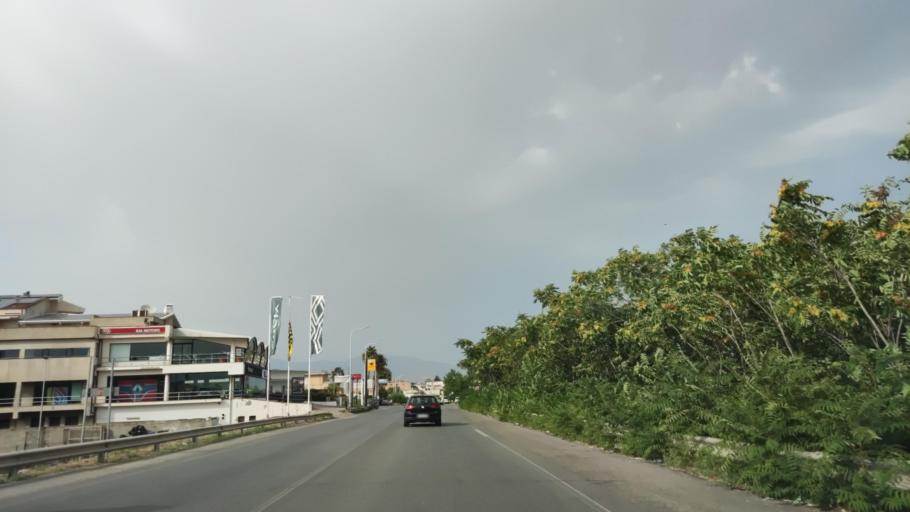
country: IT
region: Calabria
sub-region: Provincia di Reggio Calabria
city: Siderno
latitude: 38.2536
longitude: 16.2819
